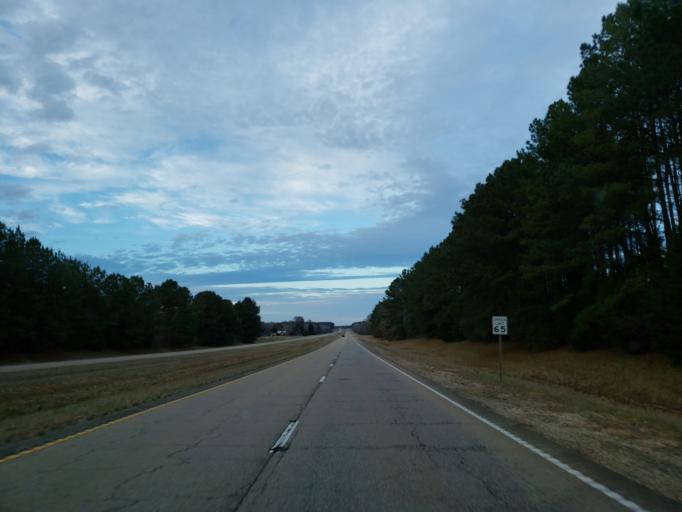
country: US
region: Mississippi
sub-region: Kemper County
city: De Kalb
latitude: 32.6890
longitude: -88.4880
